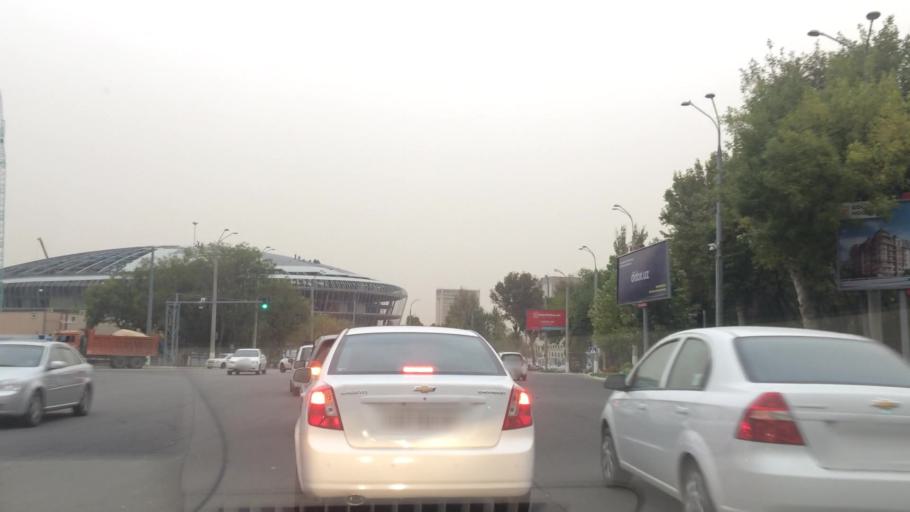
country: UZ
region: Toshkent Shahri
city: Tashkent
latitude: 41.3078
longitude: 69.2558
